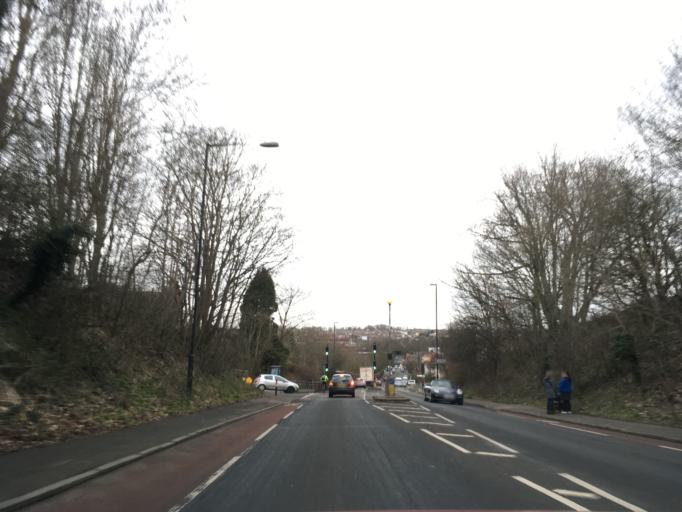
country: GB
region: England
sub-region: Bristol
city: Bristol
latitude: 51.4774
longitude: -2.5715
